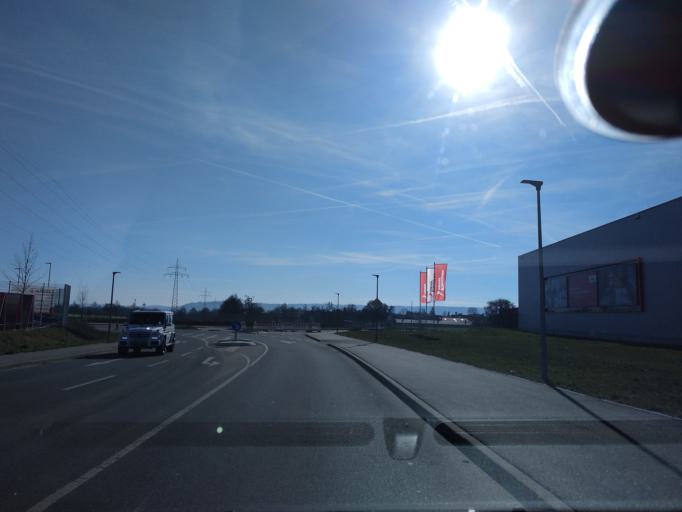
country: DE
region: Baden-Wuerttemberg
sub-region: Regierungsbezirk Stuttgart
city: Schwaebisch Hall
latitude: 49.0971
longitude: 9.7118
